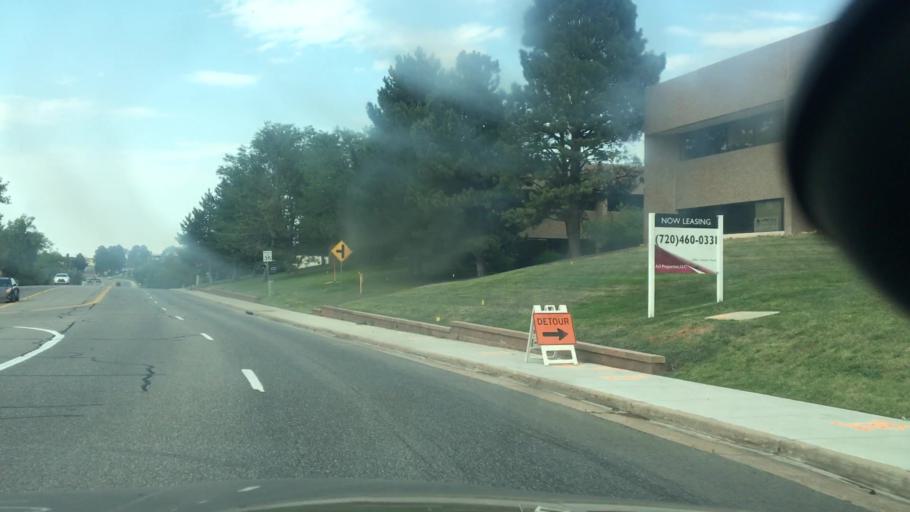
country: US
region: Colorado
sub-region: Arapahoe County
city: Centennial
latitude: 39.5865
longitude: -104.8854
